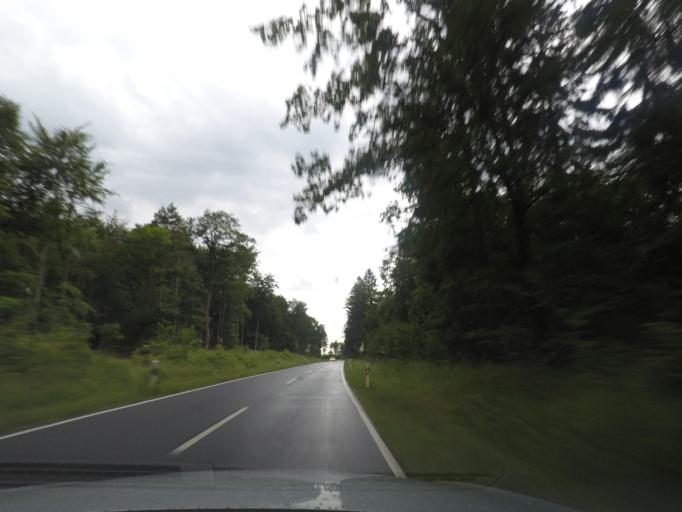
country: DE
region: Lower Saxony
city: Warberg
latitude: 52.1607
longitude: 10.9124
